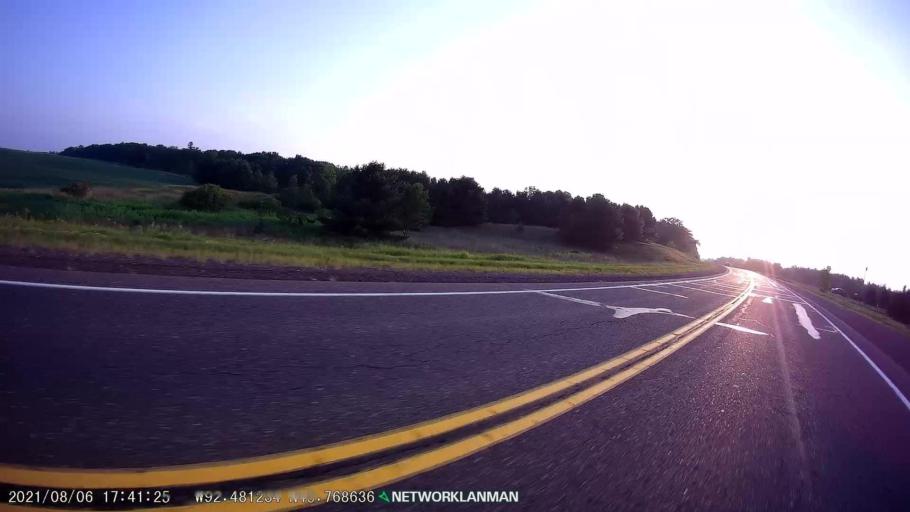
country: US
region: Wisconsin
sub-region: Burnett County
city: Siren
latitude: 45.7684
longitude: -92.4827
